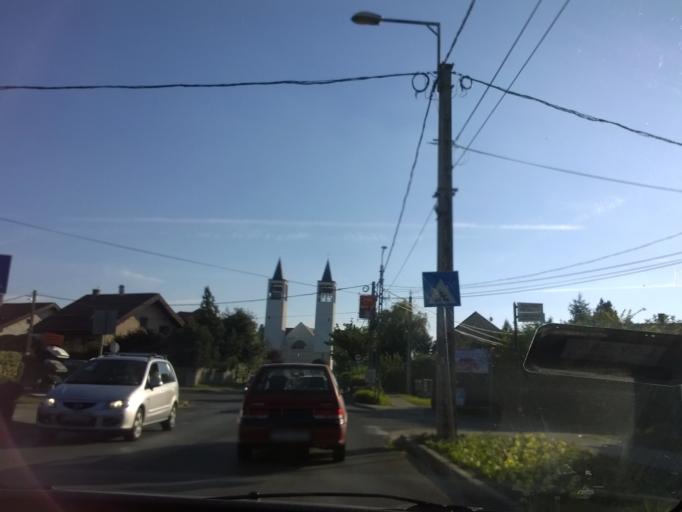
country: HU
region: Pest
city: Szigetszentmiklos
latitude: 47.3472
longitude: 19.0415
